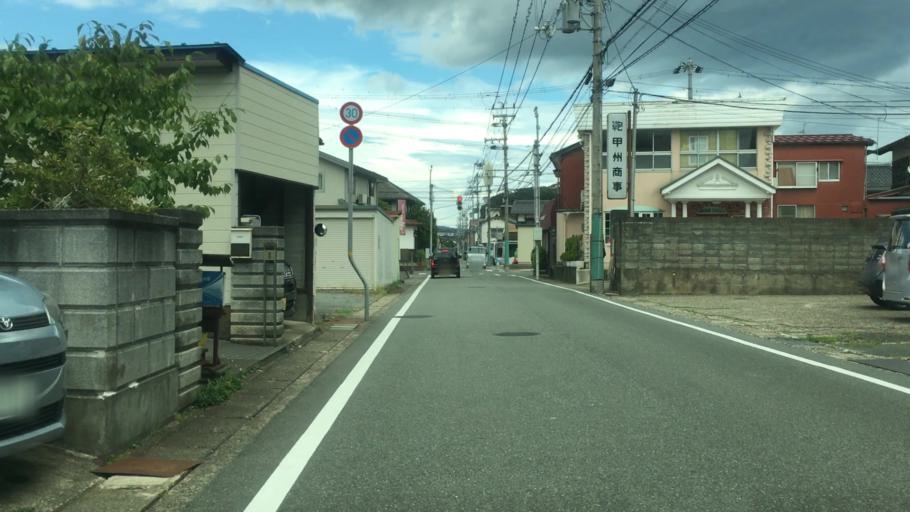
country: JP
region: Hyogo
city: Toyooka
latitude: 35.5342
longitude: 134.8205
